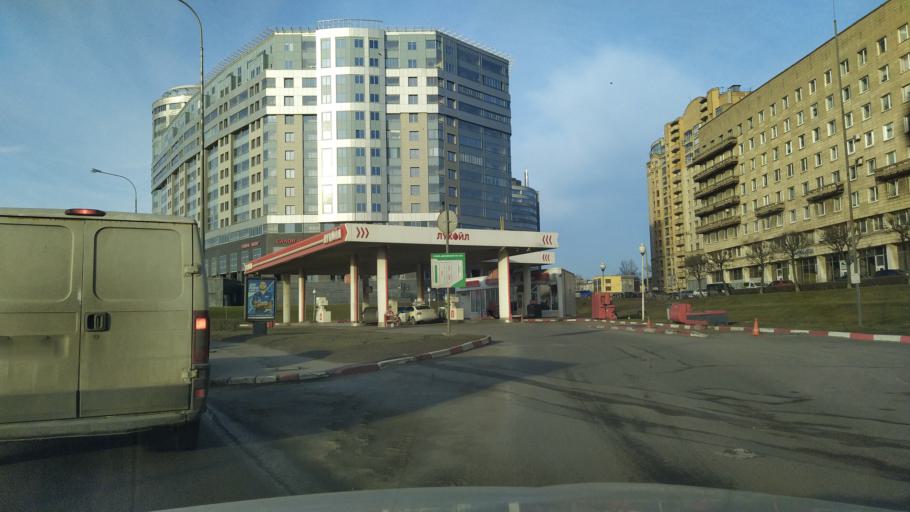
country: RU
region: Leningrad
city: Finlyandskiy
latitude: 59.9544
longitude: 30.4077
